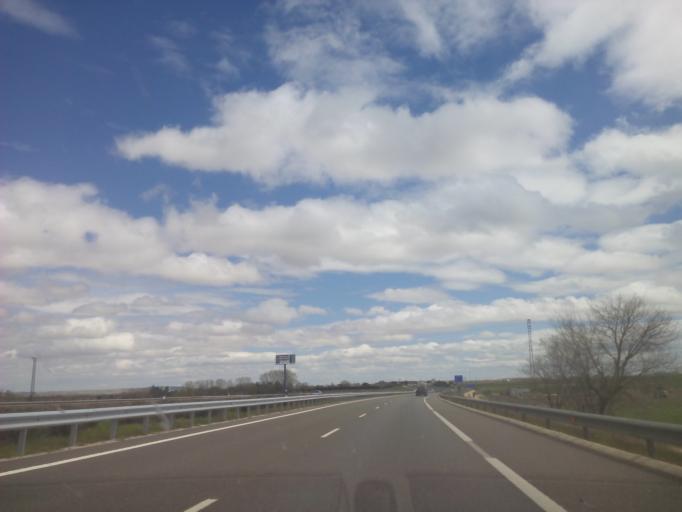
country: ES
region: Castille and Leon
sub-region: Provincia de Salamanca
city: Santa Marta de Tormes
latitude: 40.9443
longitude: -5.6192
